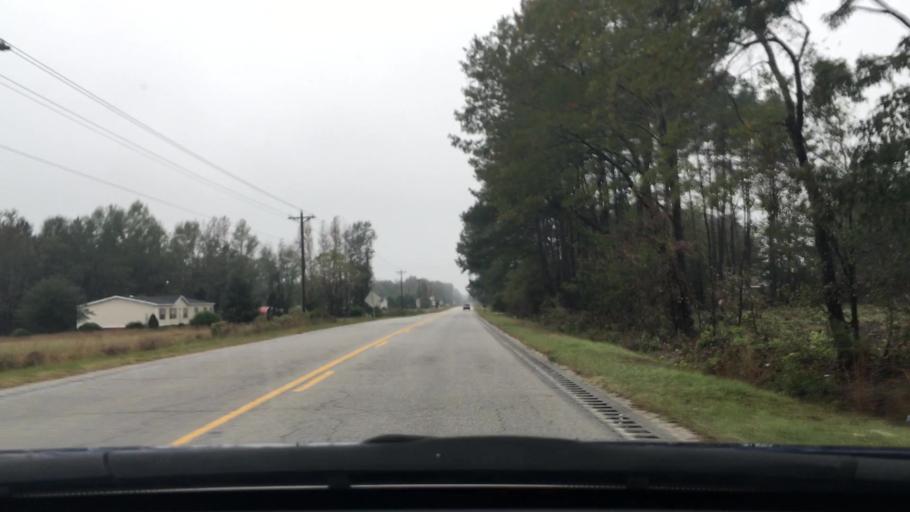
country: US
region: South Carolina
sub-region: Florence County
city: Timmonsville
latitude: 34.2316
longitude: -79.9822
